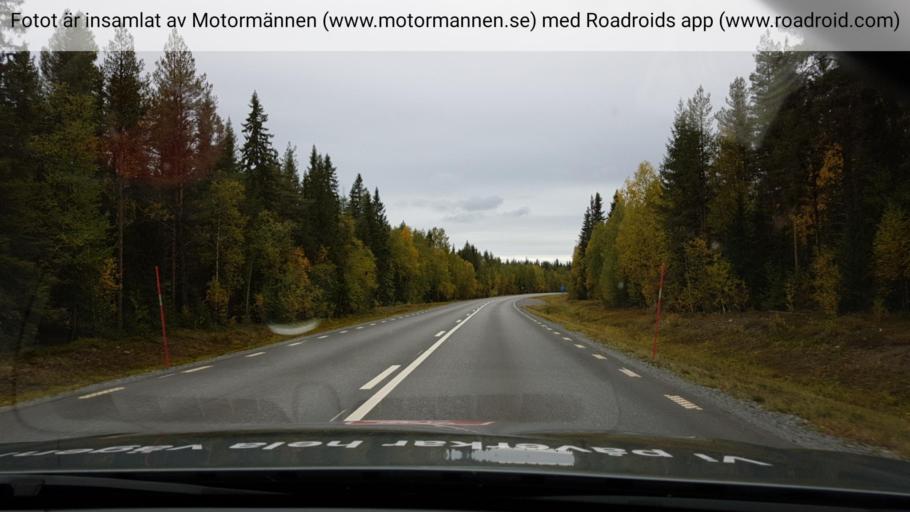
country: SE
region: Vaesterbotten
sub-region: Dorotea Kommun
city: Dorotea
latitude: 64.3064
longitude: 16.5946
